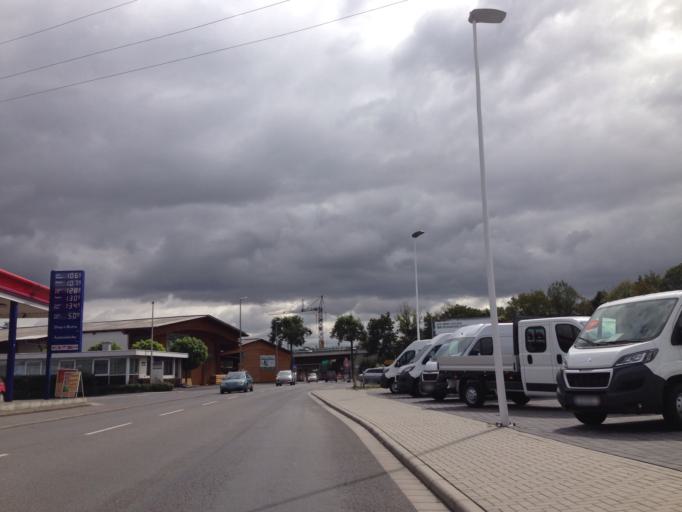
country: DE
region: Hesse
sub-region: Regierungsbezirk Giessen
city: Elz
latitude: 50.4052
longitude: 8.0386
